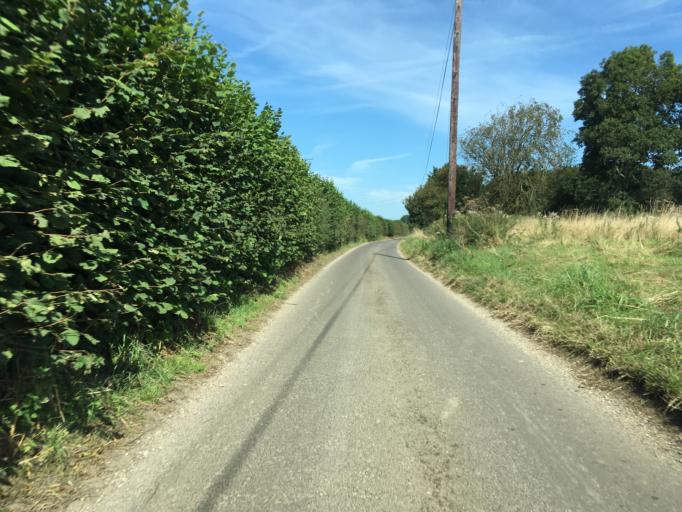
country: GB
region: England
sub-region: Hampshire
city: Highclere
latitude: 51.3043
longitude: -1.3837
